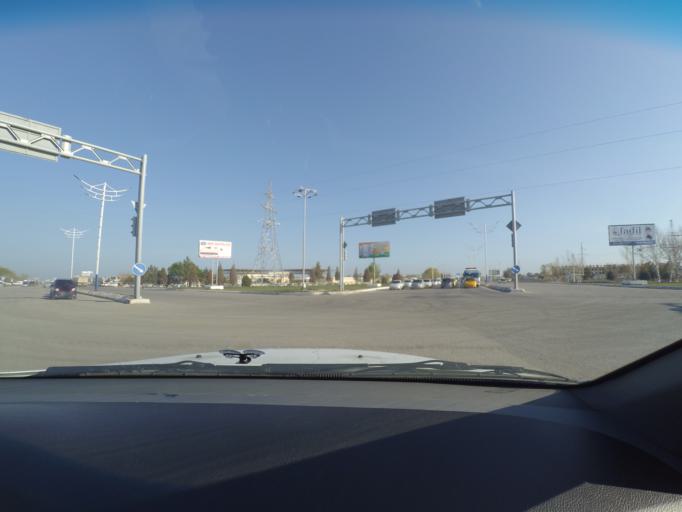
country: UZ
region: Bukhara
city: Bukhara
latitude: 39.8032
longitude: 64.4277
